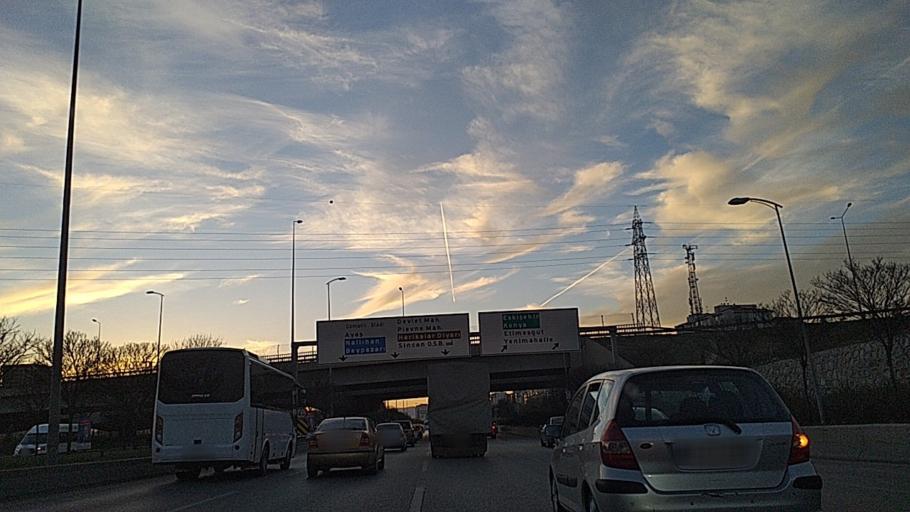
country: TR
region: Ankara
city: Etimesgut
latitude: 39.9668
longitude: 32.6311
